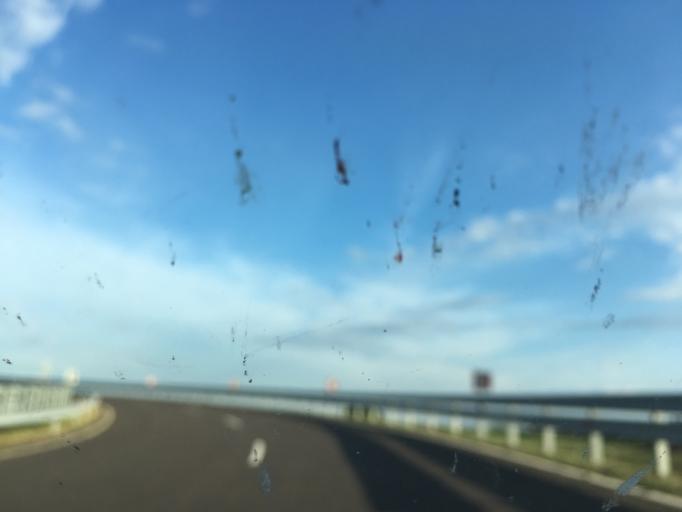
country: HU
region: Hajdu-Bihar
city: Debrecen
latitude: 47.5622
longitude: 21.5460
